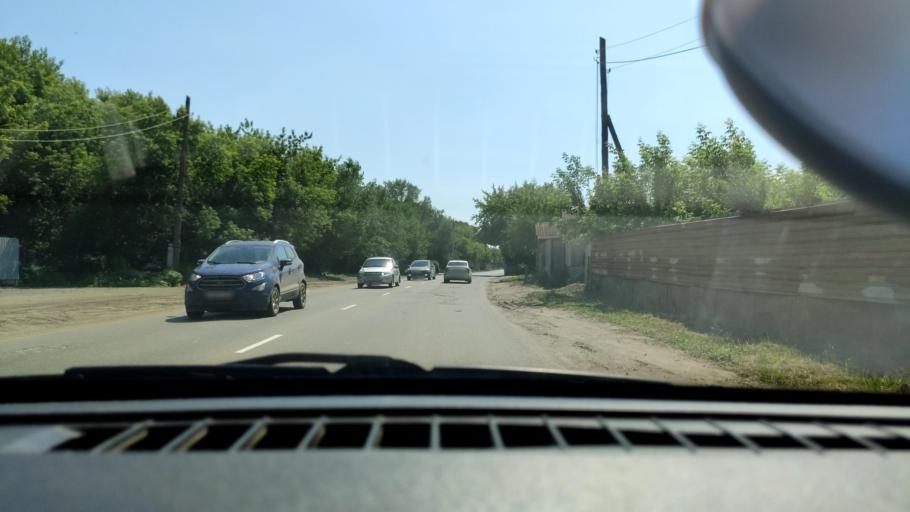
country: RU
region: Samara
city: Rozhdestveno
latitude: 53.1225
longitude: 50.0588
